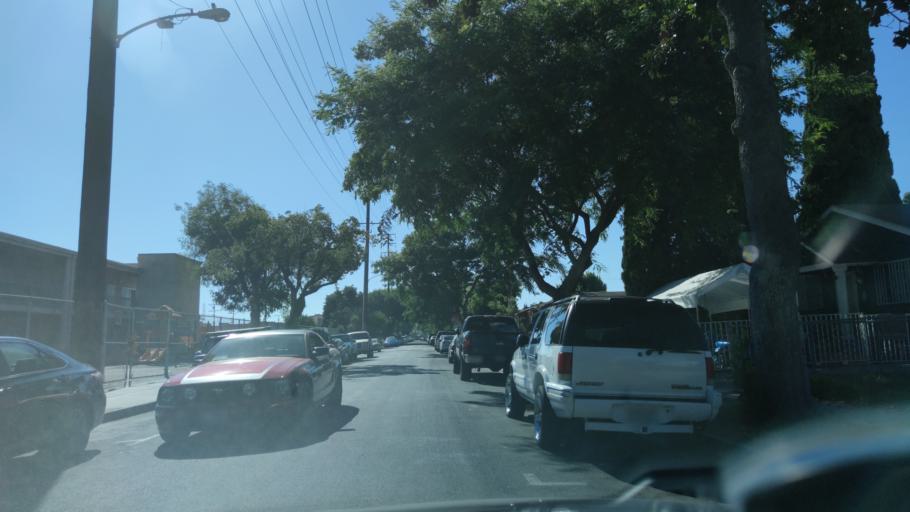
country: US
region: California
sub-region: Los Angeles County
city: Maywood
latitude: 33.9906
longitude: -118.1997
